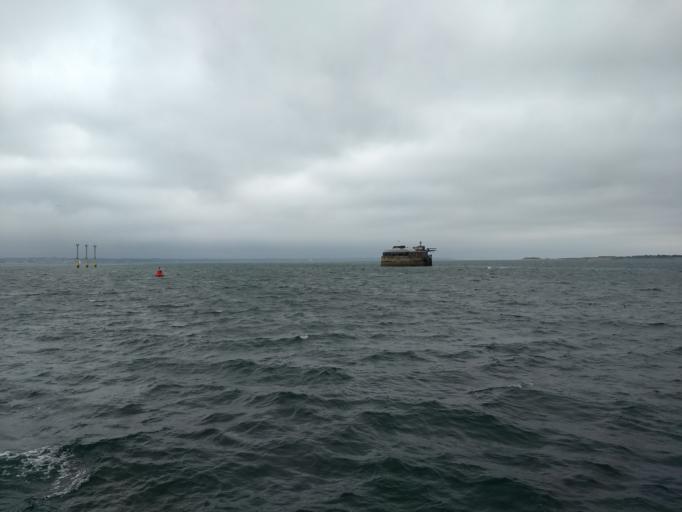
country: GB
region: England
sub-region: Portsmouth
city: Southsea
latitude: 50.7711
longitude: -1.0918
